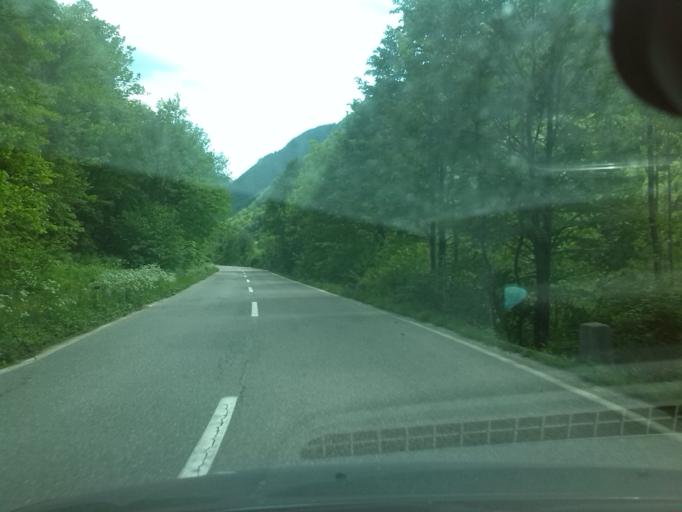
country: IT
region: Friuli Venezia Giulia
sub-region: Provincia di Udine
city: Pulfero
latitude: 46.2399
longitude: 13.5030
